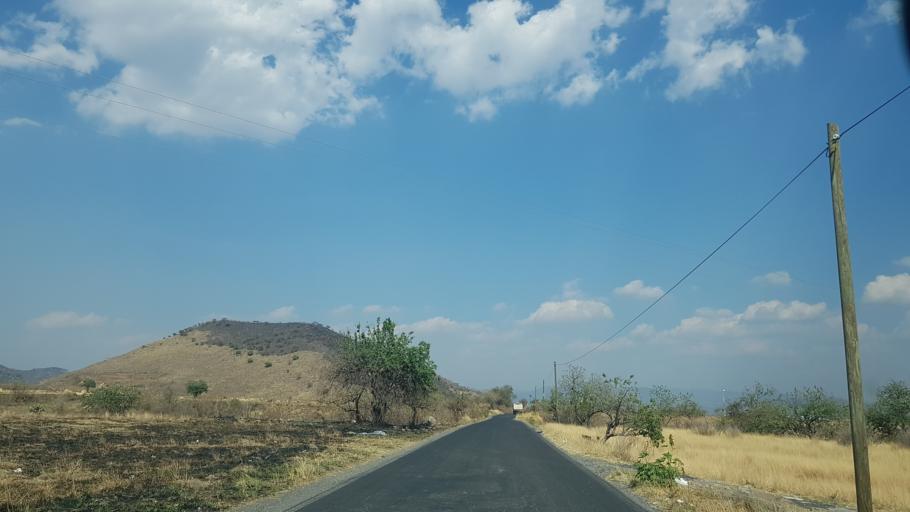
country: MX
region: Puebla
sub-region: Tianguismanalco
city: San Martin Tlapala
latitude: 18.9236
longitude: -98.4867
